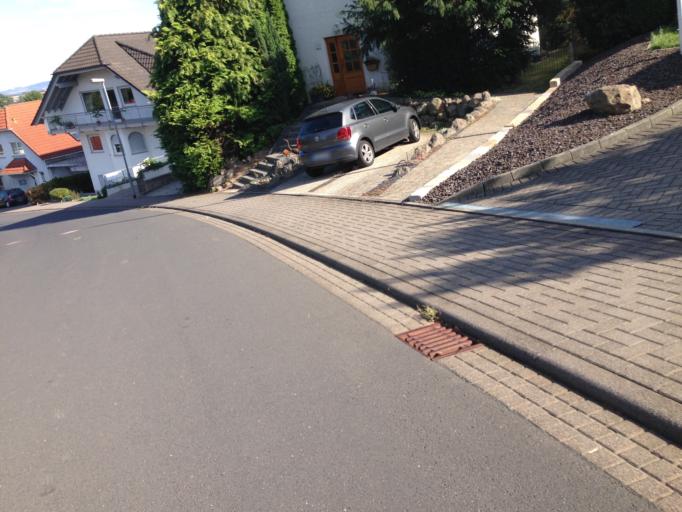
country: DE
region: Hesse
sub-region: Regierungsbezirk Giessen
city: Grunberg
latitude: 50.6179
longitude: 8.9057
